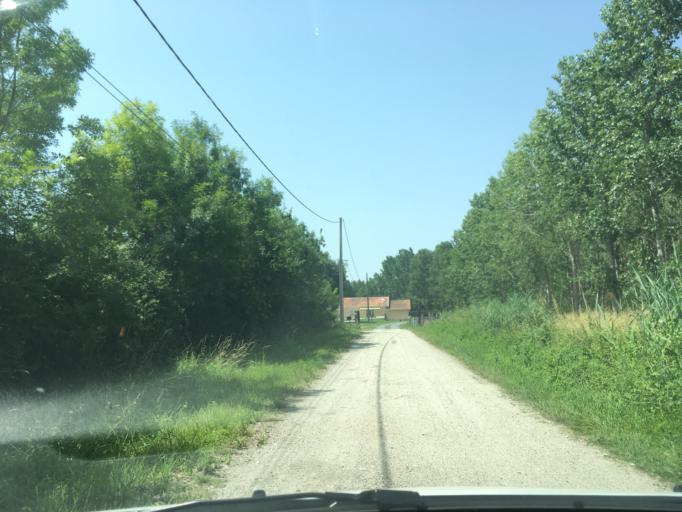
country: FR
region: Aquitaine
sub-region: Departement de la Gironde
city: Cantenac
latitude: 45.0259
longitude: -0.6387
